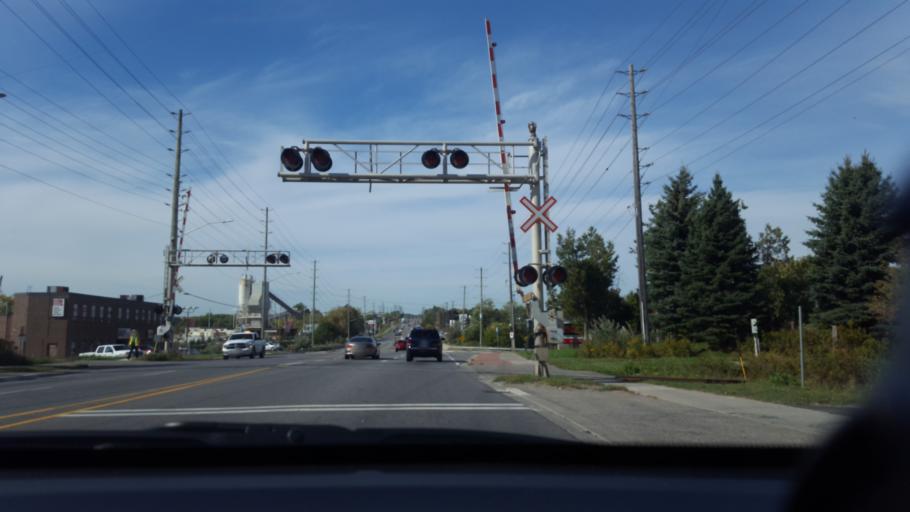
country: CA
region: Ontario
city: Newmarket
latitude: 44.0405
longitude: -79.4574
